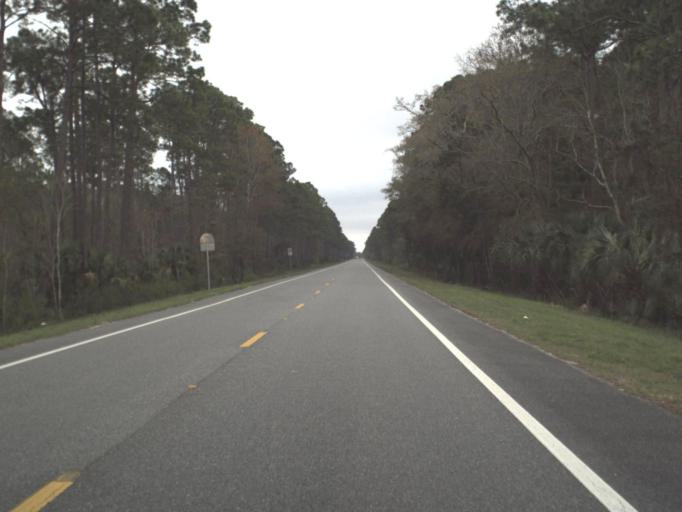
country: US
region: Florida
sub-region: Franklin County
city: Eastpoint
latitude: 29.8190
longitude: -84.8495
